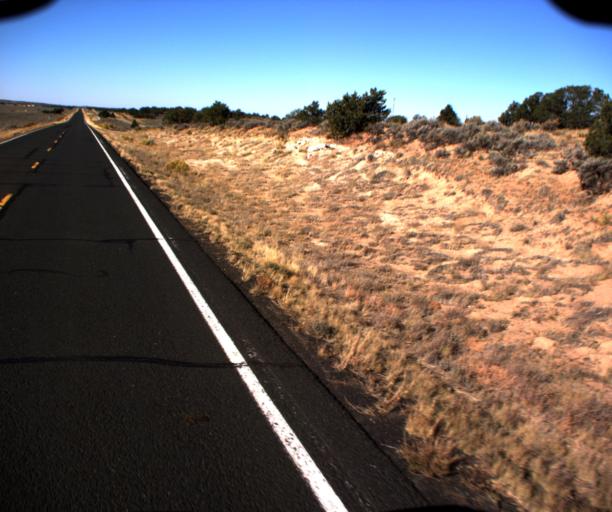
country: US
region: Arizona
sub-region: Navajo County
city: First Mesa
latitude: 35.7404
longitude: -110.0751
